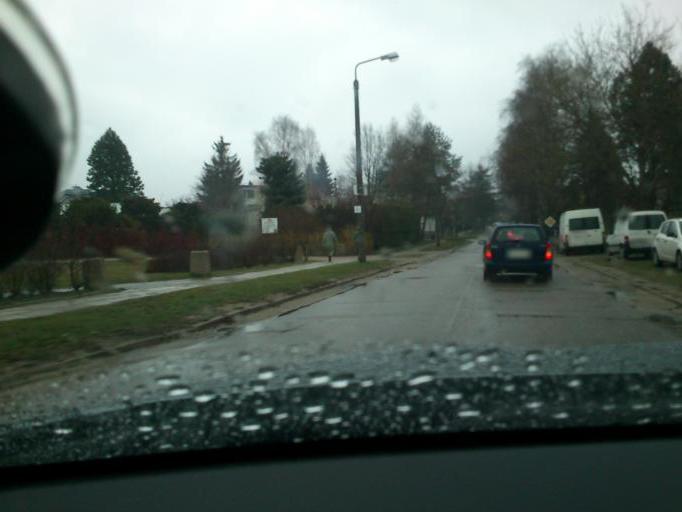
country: PL
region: Pomeranian Voivodeship
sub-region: Gdynia
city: Wielki Kack
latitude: 54.4254
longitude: 18.4678
